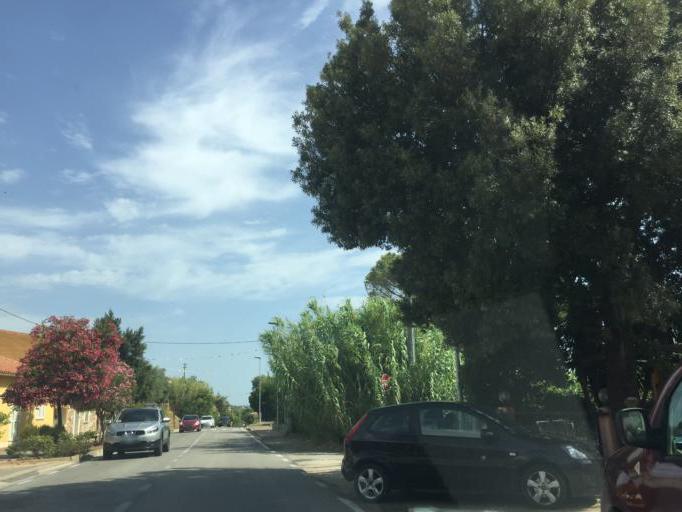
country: IT
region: Sardinia
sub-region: Provincia di Olbia-Tempio
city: San Teodoro
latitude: 40.7435
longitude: 9.6465
